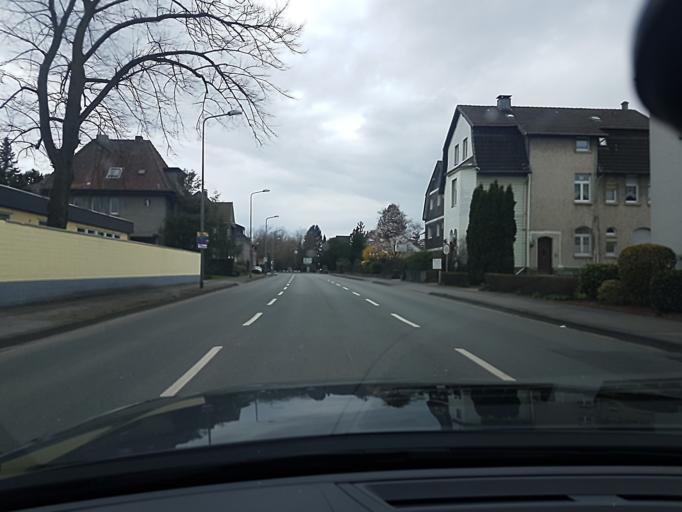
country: DE
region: North Rhine-Westphalia
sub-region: Regierungsbezirk Arnsberg
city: Unna
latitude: 51.5385
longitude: 7.6847
